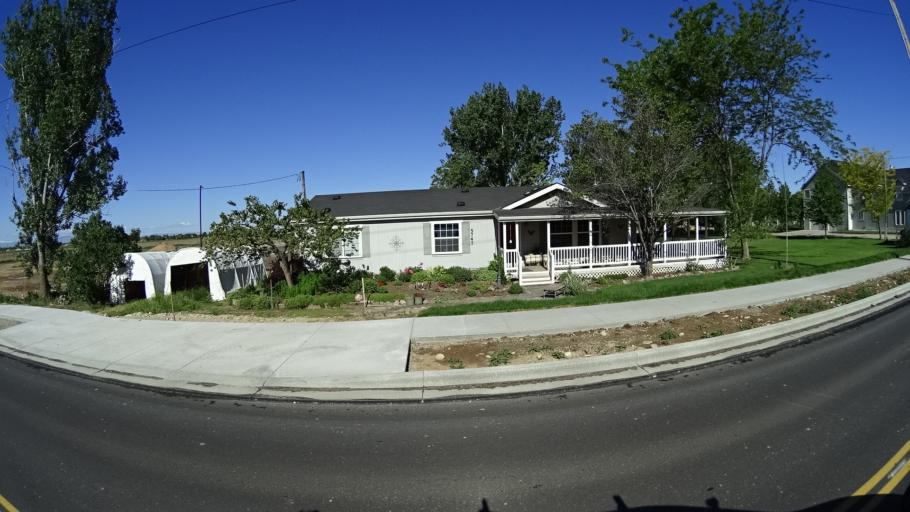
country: US
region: Idaho
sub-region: Ada County
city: Meridian
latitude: 43.6562
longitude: -116.4337
